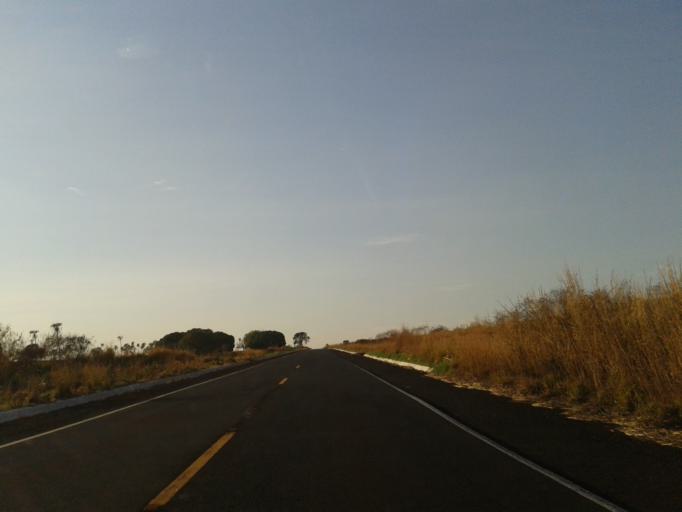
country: BR
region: Minas Gerais
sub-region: Santa Vitoria
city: Santa Vitoria
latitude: -19.1139
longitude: -50.3136
